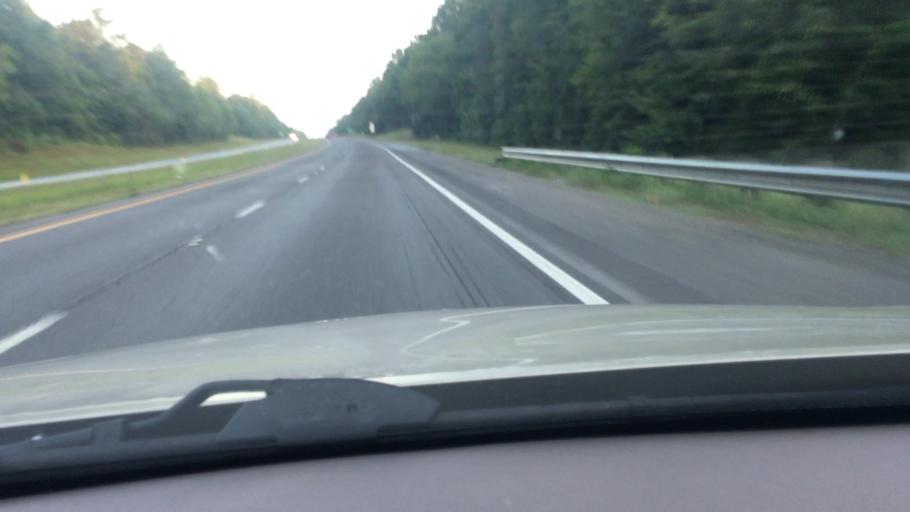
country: US
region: South Carolina
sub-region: Richland County
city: Lake Murray of Richland
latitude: 34.1487
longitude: -81.2438
